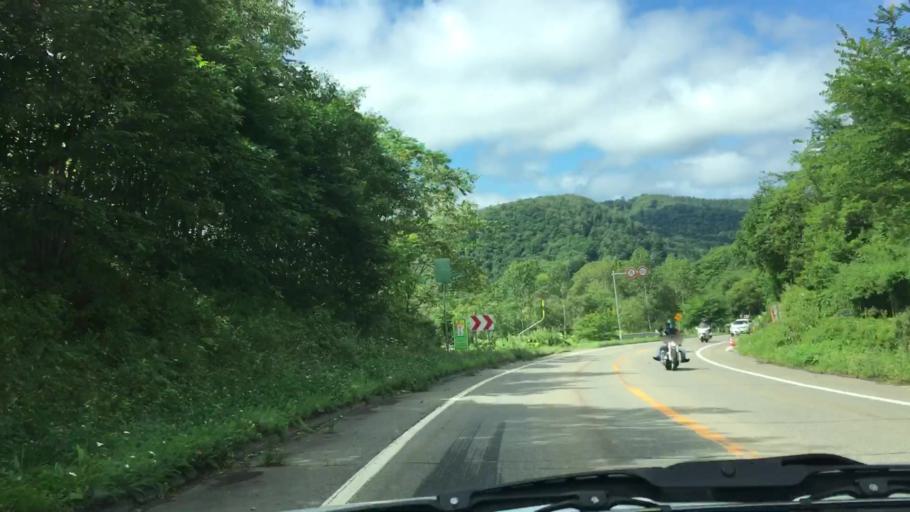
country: JP
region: Hokkaido
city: Kitami
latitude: 43.3526
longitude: 143.7943
